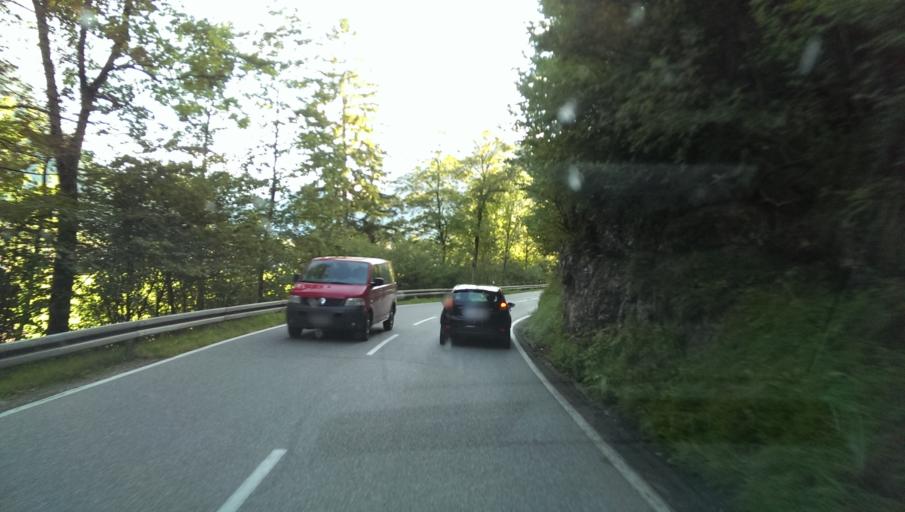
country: DE
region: Bavaria
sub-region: Upper Bavaria
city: Mittenwald
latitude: 47.4522
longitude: 11.2688
